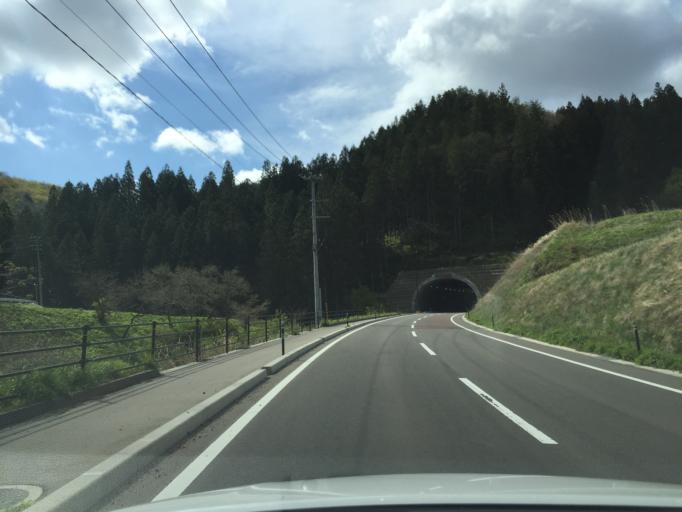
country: JP
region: Fukushima
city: Hobaramachi
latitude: 37.6392
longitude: 140.6433
